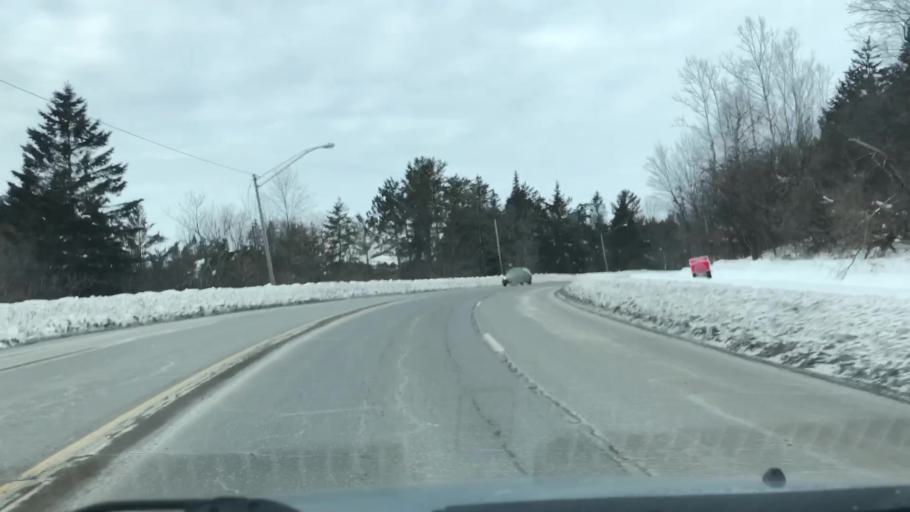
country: US
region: Minnesota
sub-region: Saint Louis County
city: Arnold
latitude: 46.8385
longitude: -92.0789
